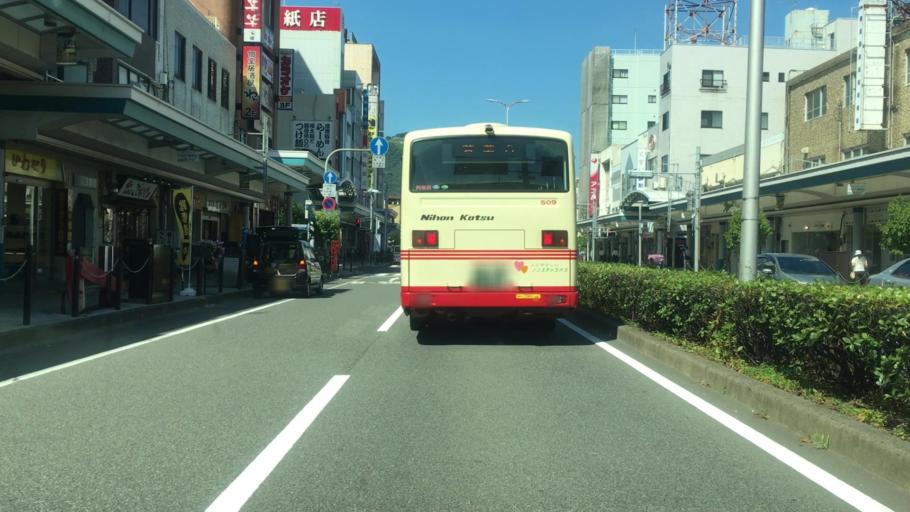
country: JP
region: Tottori
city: Tottori
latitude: 35.4949
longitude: 134.2272
